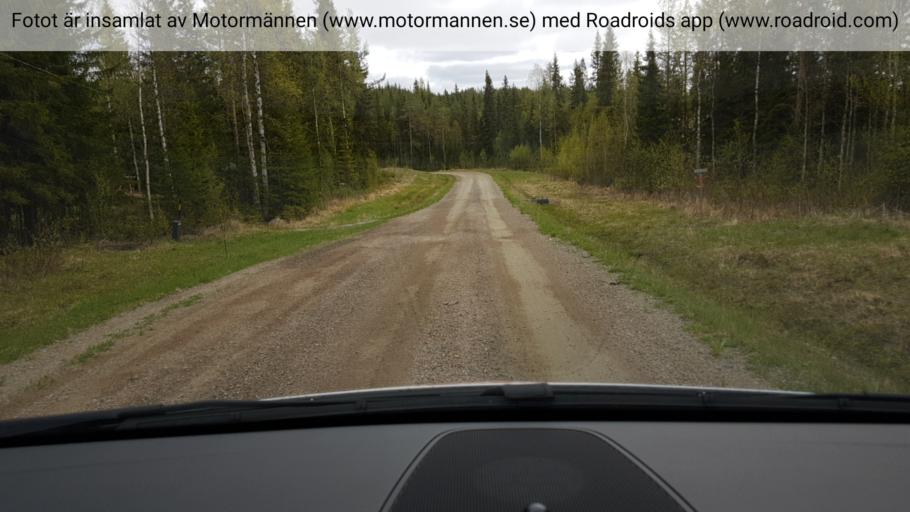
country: SE
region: Jaemtland
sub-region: Braecke Kommun
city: Braecke
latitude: 62.8017
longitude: 15.1175
